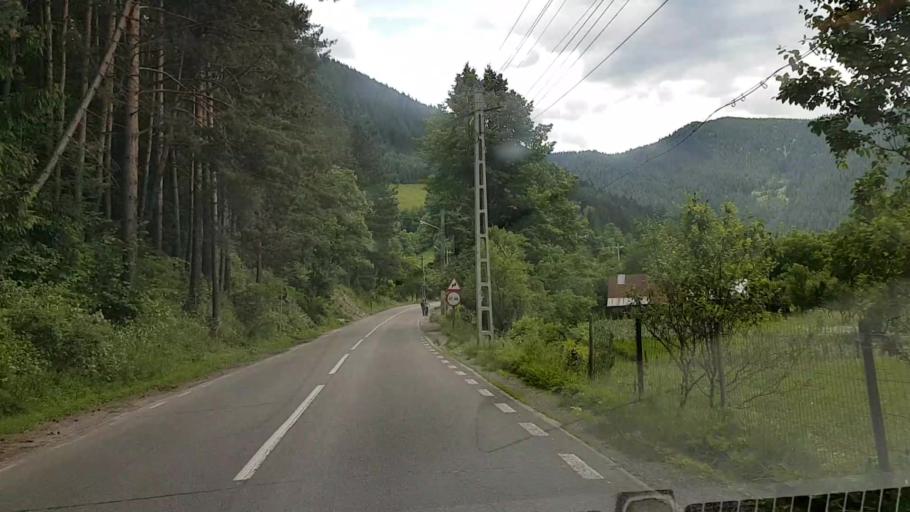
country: RO
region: Suceava
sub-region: Comuna Brosteni
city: Brosteni
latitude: 47.2305
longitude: 25.7443
